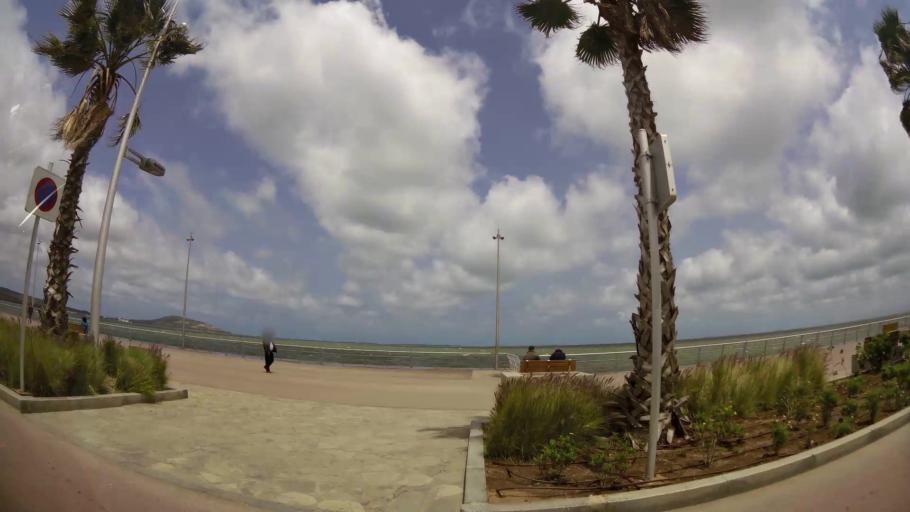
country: MA
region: Oriental
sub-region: Nador
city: Nador
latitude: 35.1788
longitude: -2.9212
